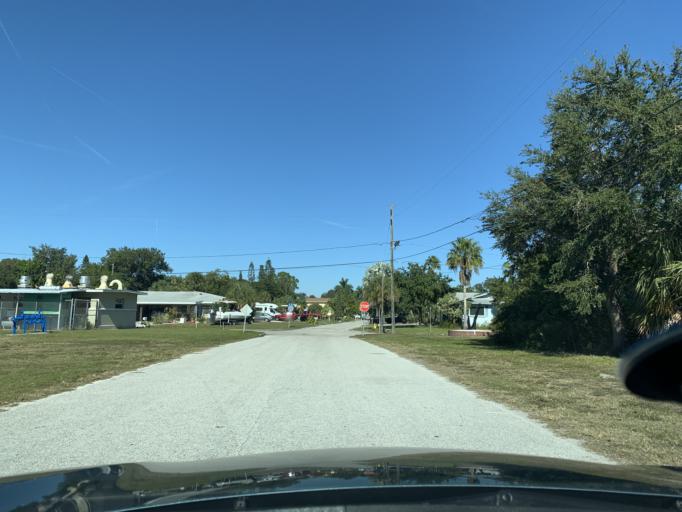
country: US
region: Florida
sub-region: Pinellas County
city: Gulfport
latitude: 27.7405
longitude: -82.6947
